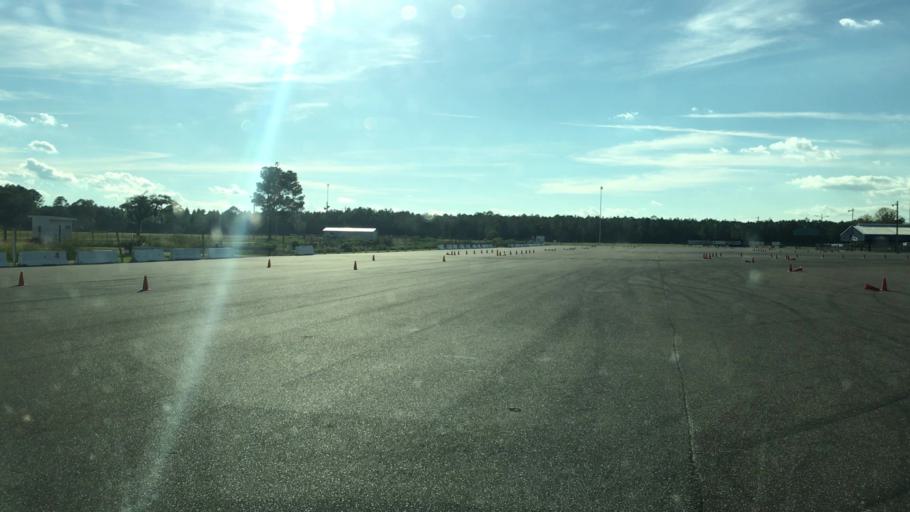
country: US
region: Florida
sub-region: Alachua County
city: Waldo
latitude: 29.7568
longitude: -82.2716
